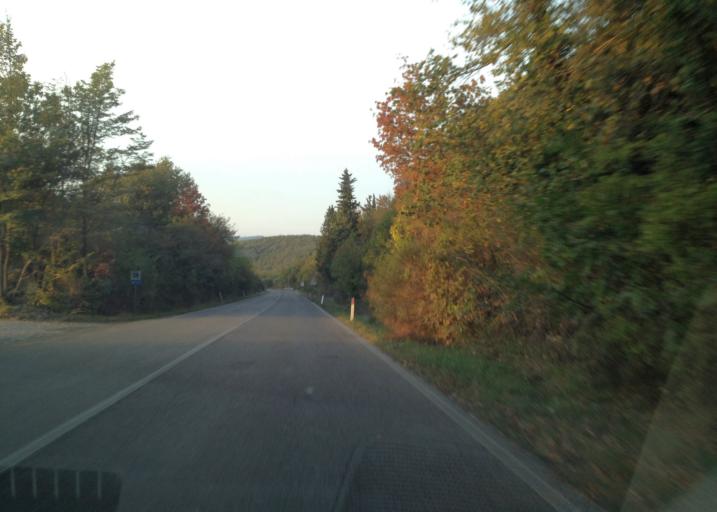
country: IT
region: Tuscany
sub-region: Provincia di Siena
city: Castellina in Chianti
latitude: 43.4942
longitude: 11.2999
